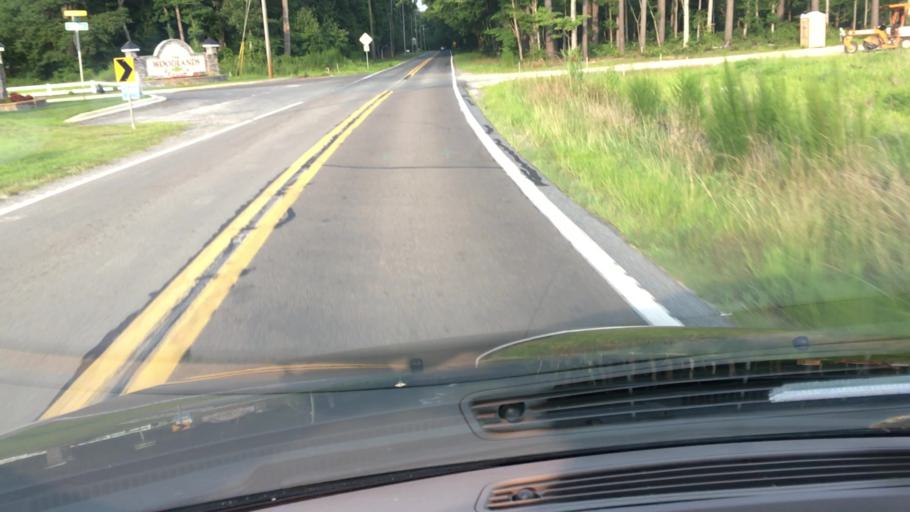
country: US
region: Delaware
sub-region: Sussex County
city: Ocean View
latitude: 38.5064
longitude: -75.1202
